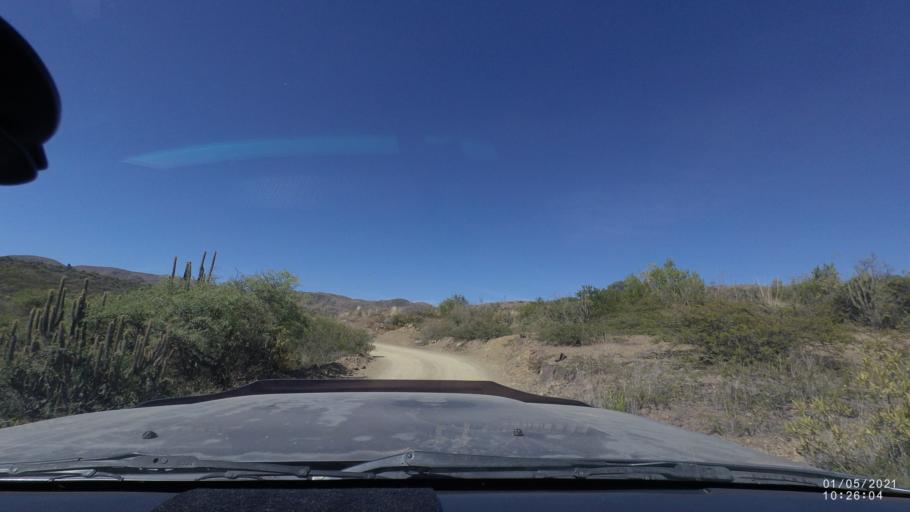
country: BO
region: Cochabamba
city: Capinota
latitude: -17.5804
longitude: -66.1926
